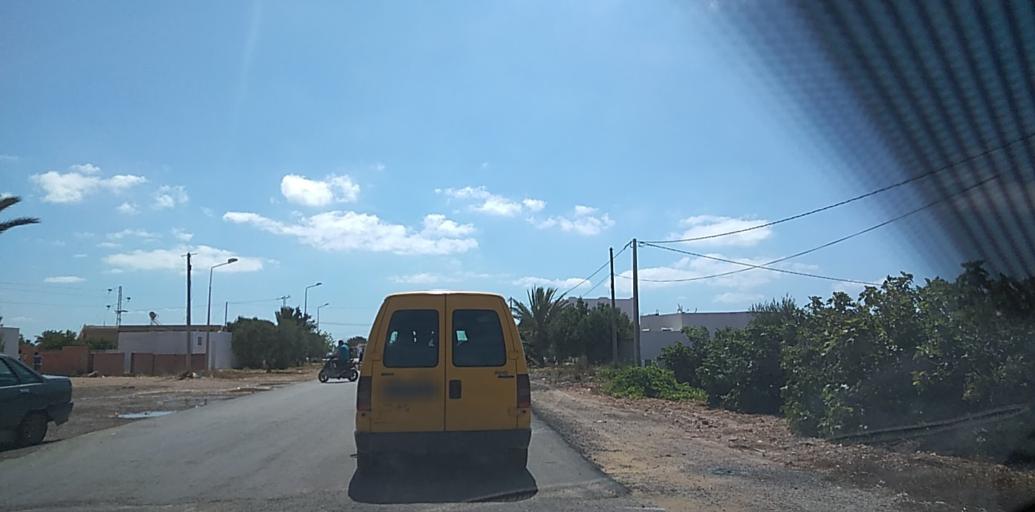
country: TN
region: Safaqis
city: Al Qarmadah
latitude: 34.6563
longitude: 11.0899
